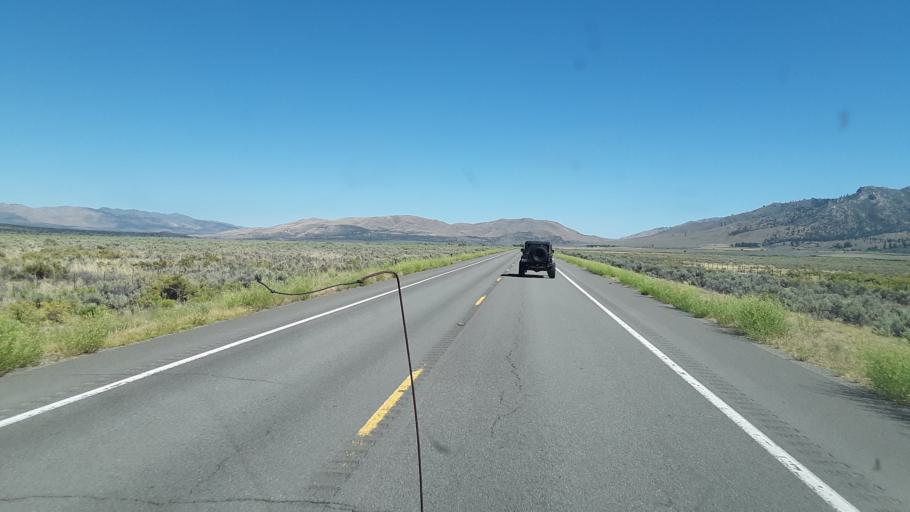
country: US
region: Nevada
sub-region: Washoe County
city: Cold Springs
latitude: 39.9898
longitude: -120.0728
